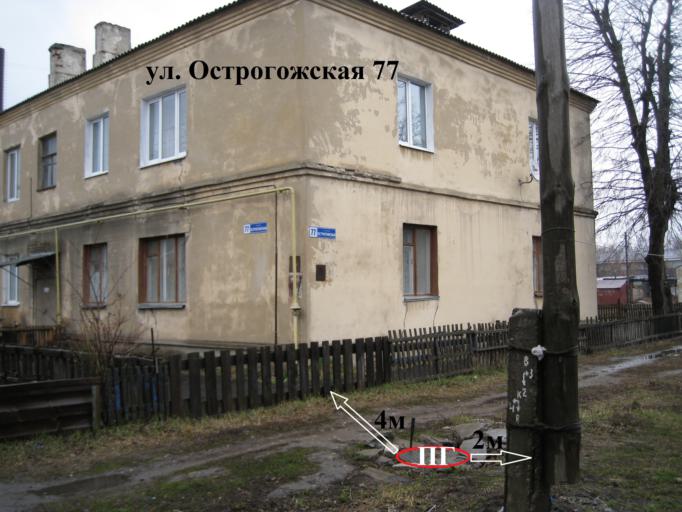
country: RU
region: Voronezj
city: Voronezh
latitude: 51.6243
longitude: 39.1770
